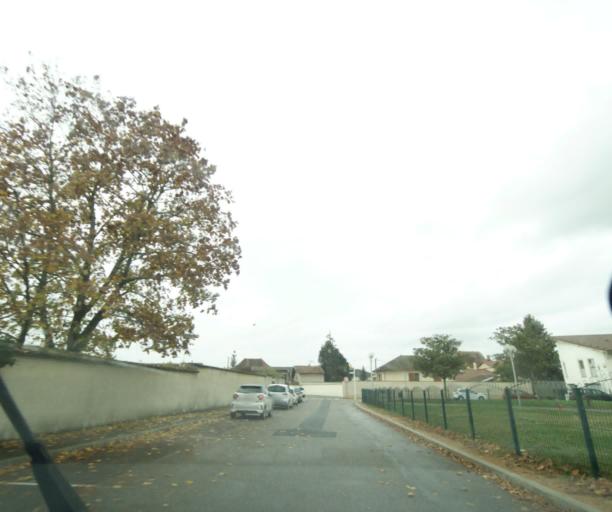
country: FR
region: Rhone-Alpes
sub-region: Departement de l'Ain
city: Loyettes
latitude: 45.7749
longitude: 5.2054
